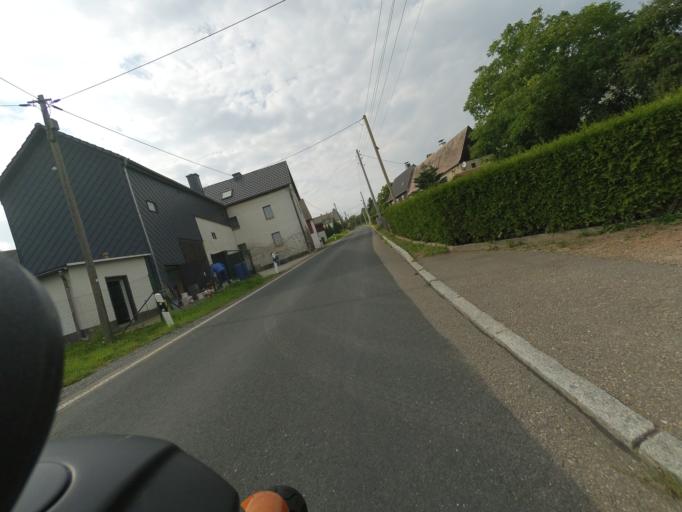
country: DE
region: Saxony
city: Barenstein
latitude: 50.8161
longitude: 13.8184
